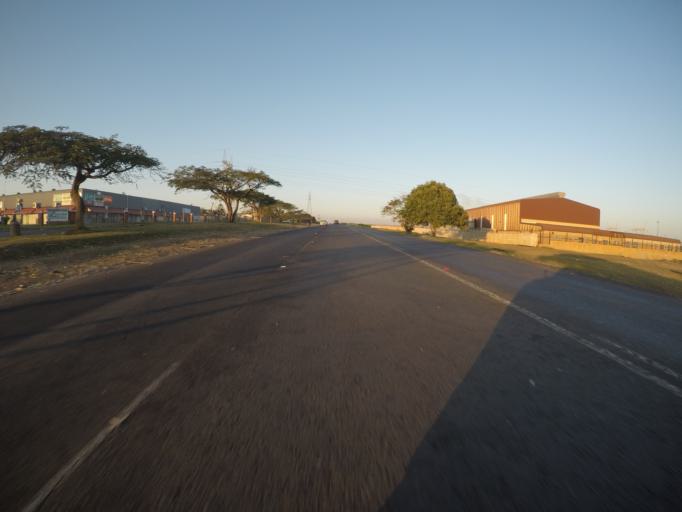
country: ZA
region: KwaZulu-Natal
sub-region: uThungulu District Municipality
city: Empangeni
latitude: -28.7802
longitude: 31.8987
